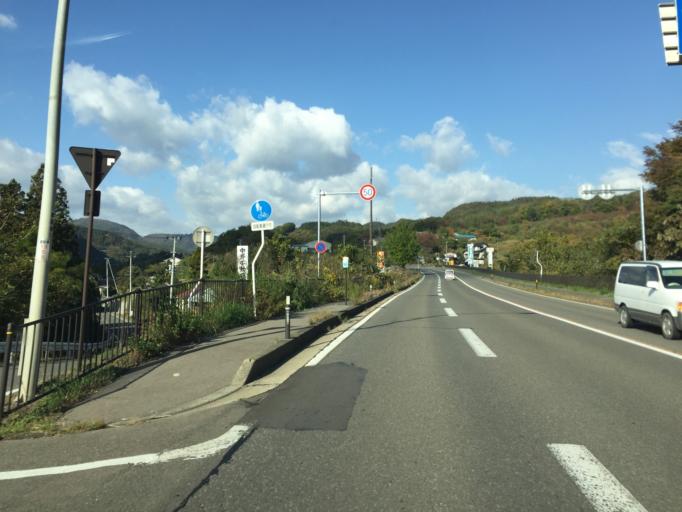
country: JP
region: Fukushima
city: Fukushima-shi
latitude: 37.8258
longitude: 140.4226
